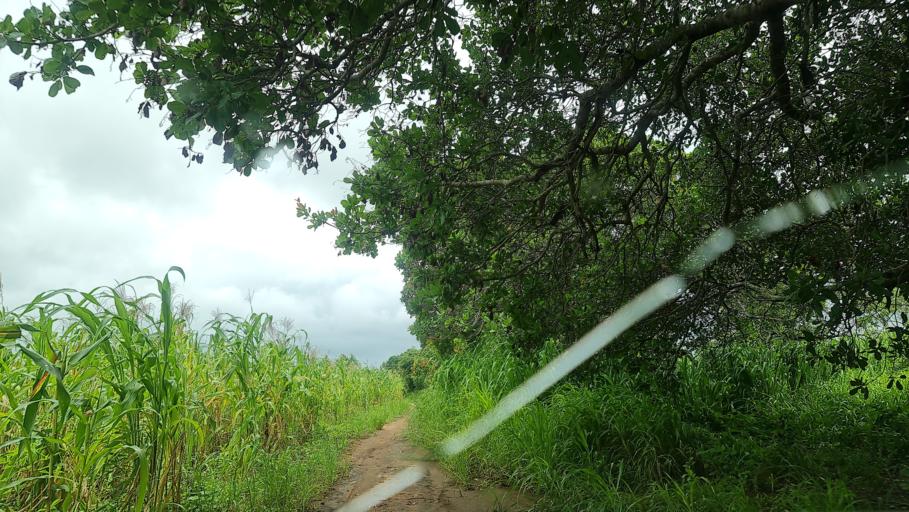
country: MW
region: Southern Region
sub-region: Nsanje District
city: Nsanje
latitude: -17.3905
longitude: 35.7818
